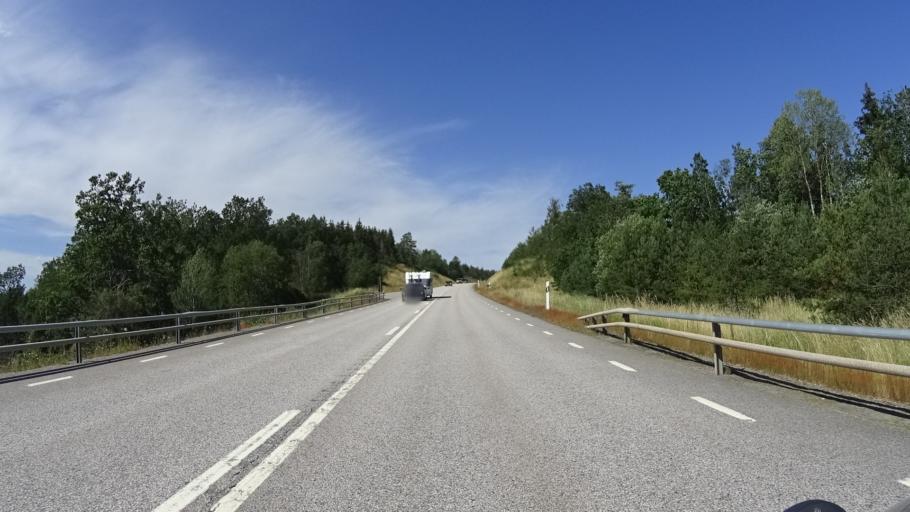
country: SE
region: Kalmar
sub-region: Vasterviks Kommun
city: Gamleby
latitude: 57.9194
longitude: 16.3749
